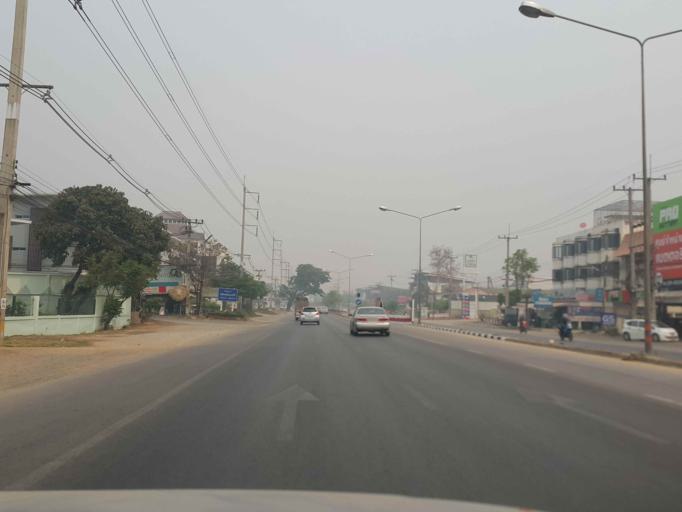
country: TH
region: Chiang Mai
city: San Sai
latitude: 18.8700
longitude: 99.0154
